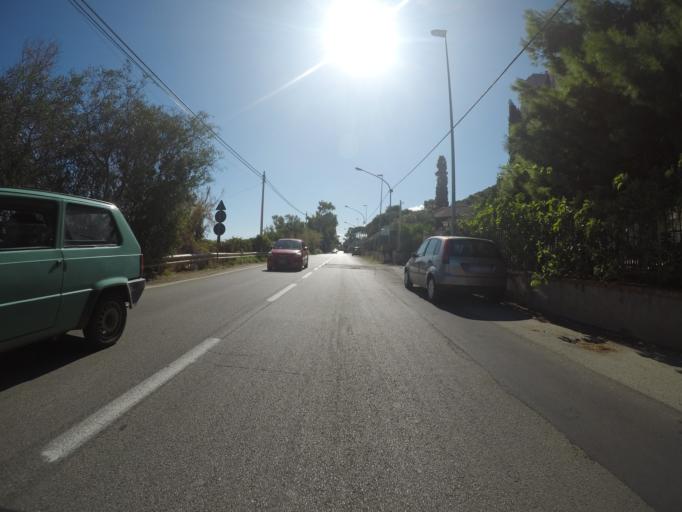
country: IT
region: Sicily
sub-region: Palermo
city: Palermo
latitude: 38.1858
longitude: 13.3617
